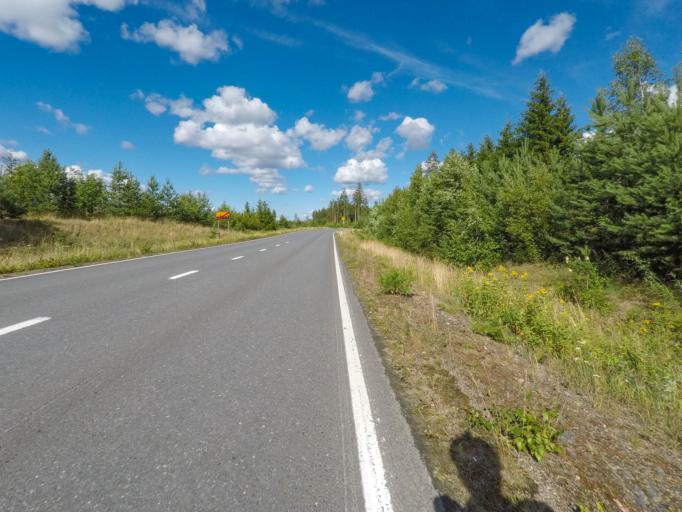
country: FI
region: South Karelia
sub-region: Lappeenranta
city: Joutseno
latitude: 61.0948
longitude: 28.3548
